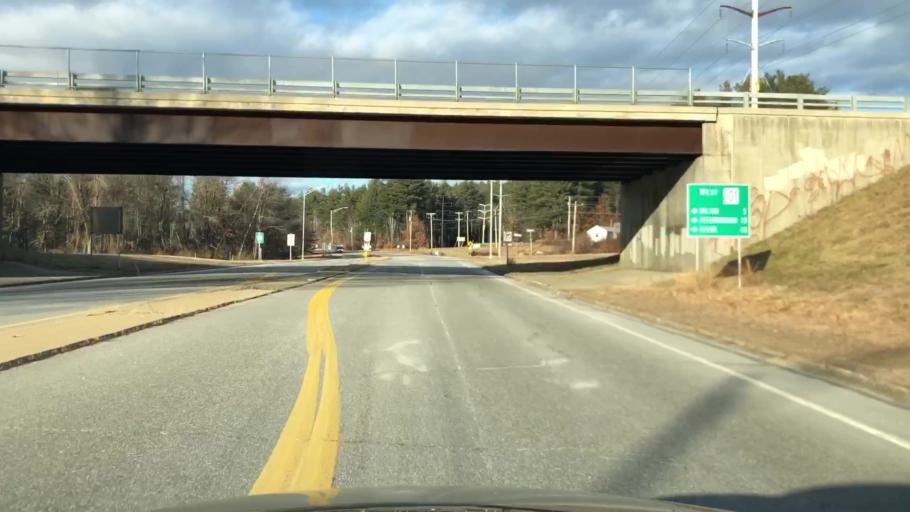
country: US
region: New Hampshire
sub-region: Hillsborough County
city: Milford
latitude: 42.8168
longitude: -71.6462
